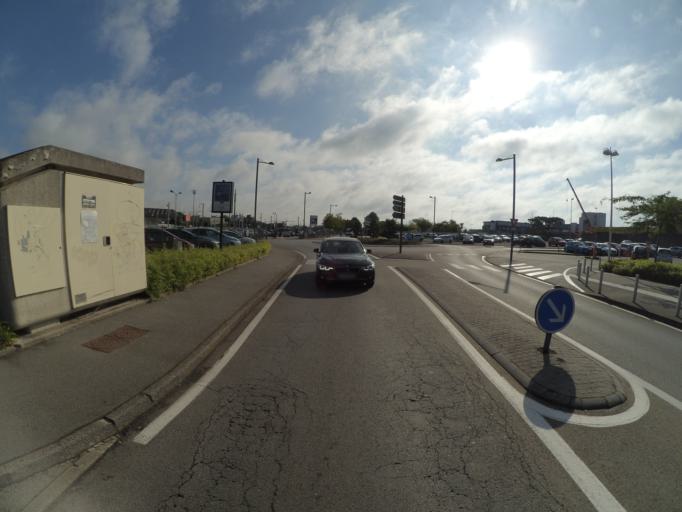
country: FR
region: Brittany
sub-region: Departement du Morbihan
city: Vannes
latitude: 47.6653
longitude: -2.7513
